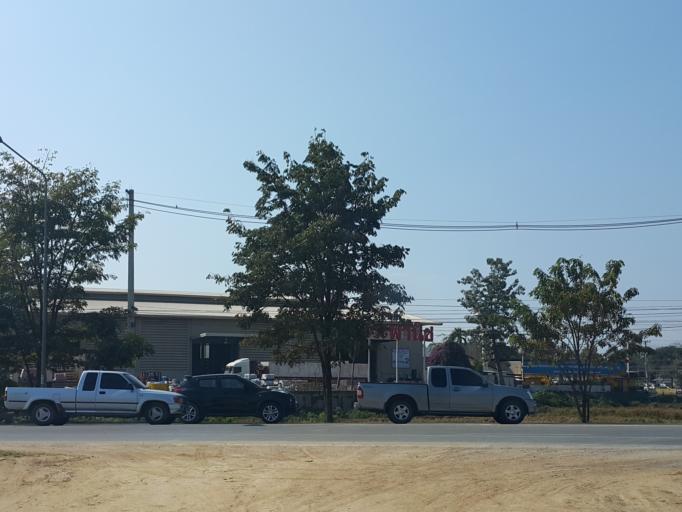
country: TH
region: Chiang Mai
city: San Sai
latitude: 18.8464
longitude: 99.0154
